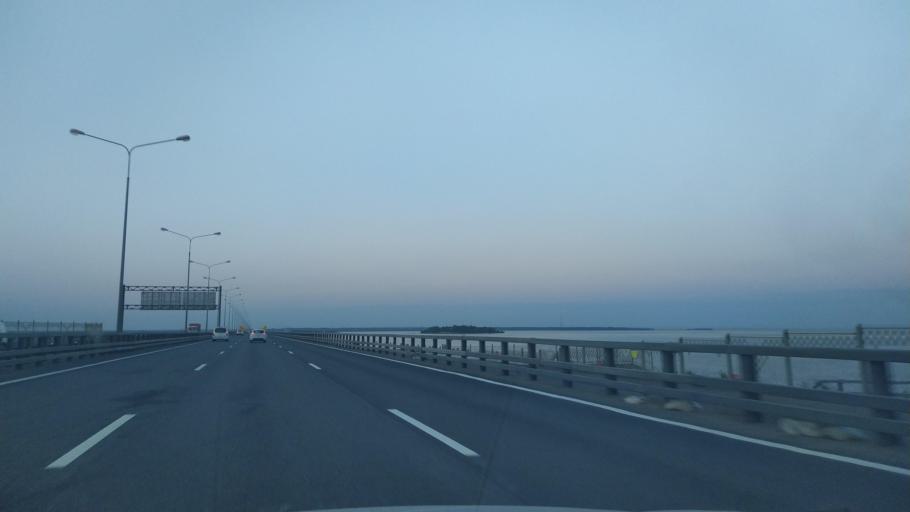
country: RU
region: Leningrad
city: Gorskaya
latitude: 60.0291
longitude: 29.8685
